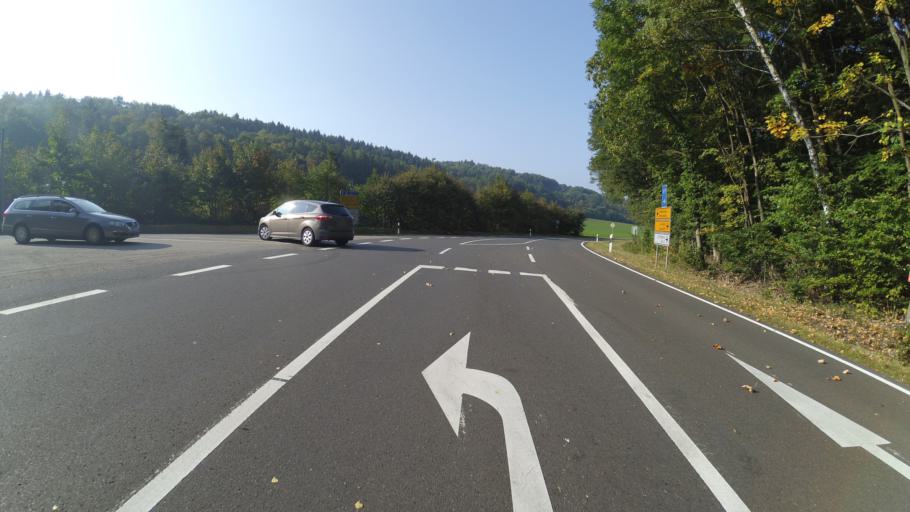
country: DE
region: Rheinland-Pfalz
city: Mittelbrunn
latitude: 49.3962
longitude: 7.5391
